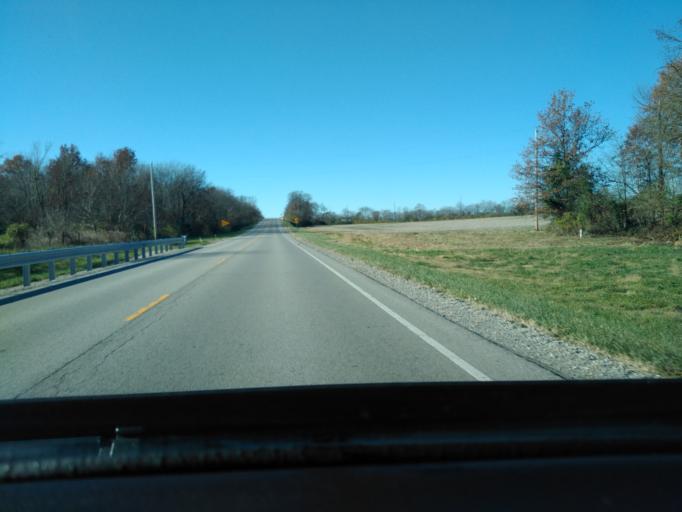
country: US
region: Illinois
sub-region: Bond County
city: Greenville
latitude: 38.8604
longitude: -89.4367
